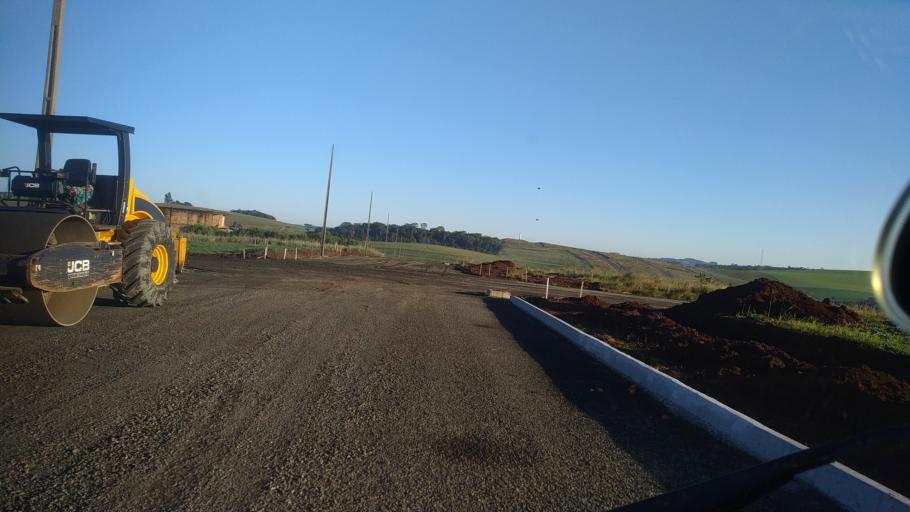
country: BR
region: Santa Catarina
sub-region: Chapeco
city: Chapeco
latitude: -27.0862
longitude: -52.6966
